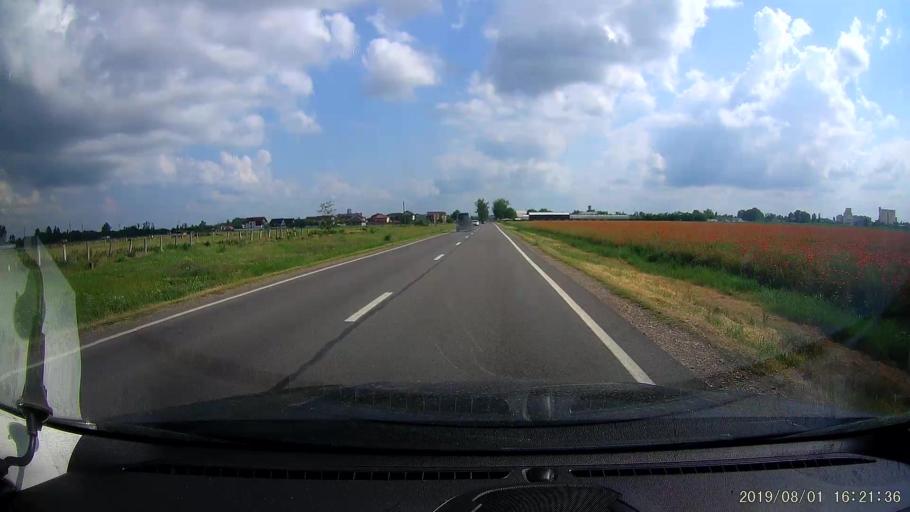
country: RO
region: Calarasi
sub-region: Municipiul Calarasi
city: Calarasi
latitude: 44.2152
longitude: 27.3397
